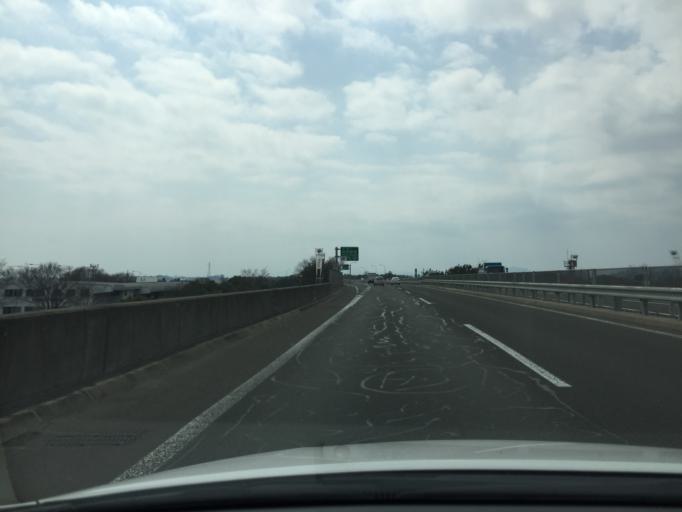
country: JP
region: Miyagi
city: Iwanuma
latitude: 38.1390
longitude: 140.8893
